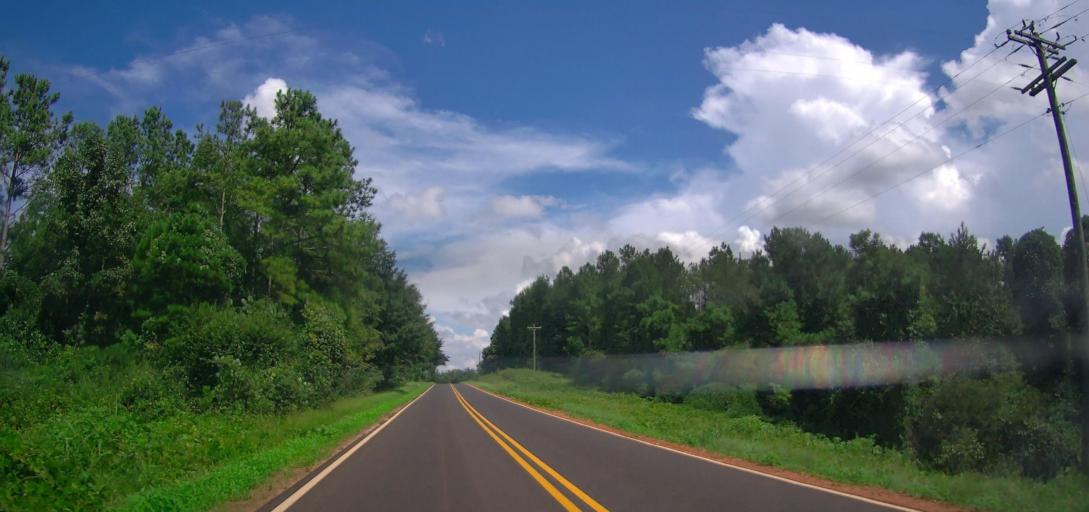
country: US
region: Georgia
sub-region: Macon County
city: Marshallville
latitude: 32.4585
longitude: -83.9166
